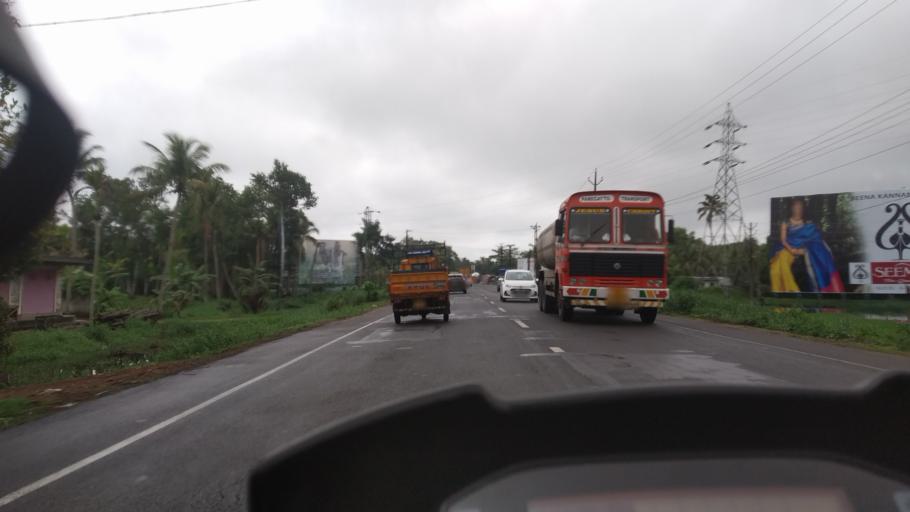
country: IN
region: Kerala
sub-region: Alappuzha
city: Mavelikara
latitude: 9.3171
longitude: 76.4181
